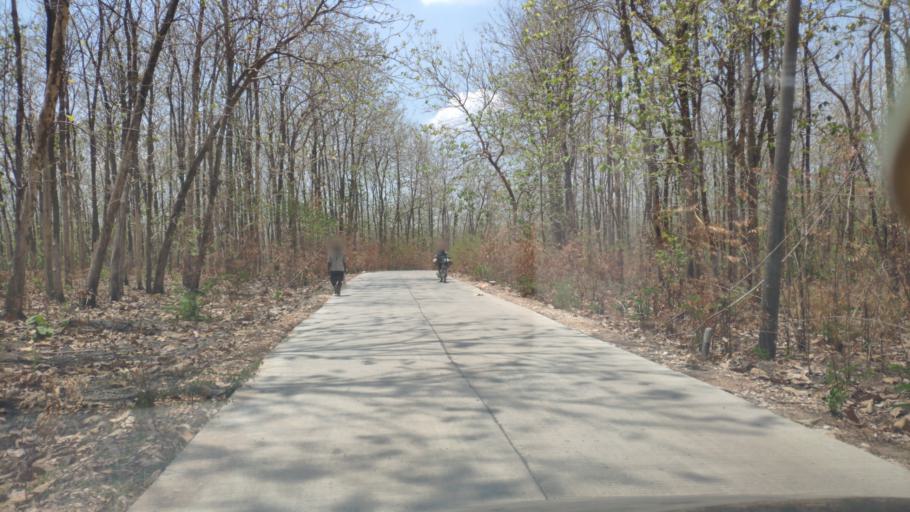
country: ID
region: Central Java
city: Randublatung
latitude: -7.2586
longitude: 111.3779
